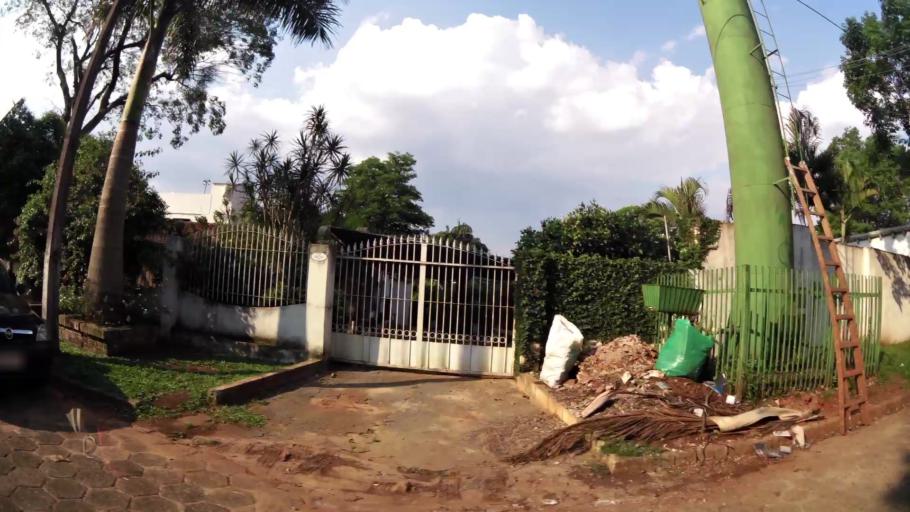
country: PY
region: Alto Parana
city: Presidente Franco
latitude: -25.5303
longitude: -54.6304
